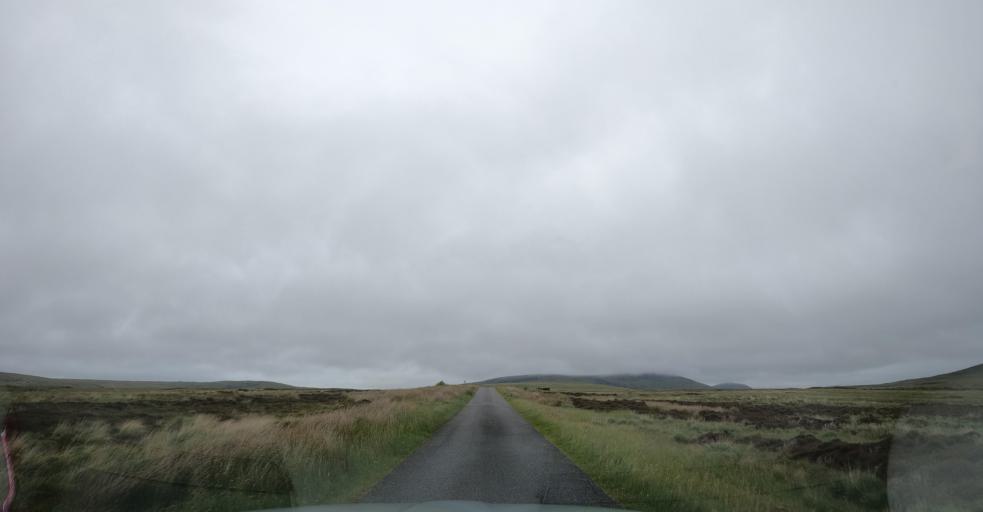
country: GB
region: Scotland
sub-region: Eilean Siar
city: Isle of North Uist
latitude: 57.5873
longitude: -7.3949
